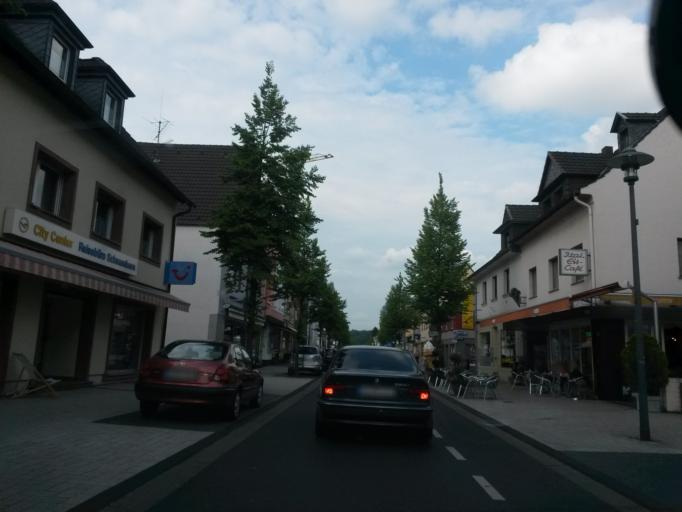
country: DE
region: North Rhine-Westphalia
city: Lohmar
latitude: 50.8402
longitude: 7.2101
